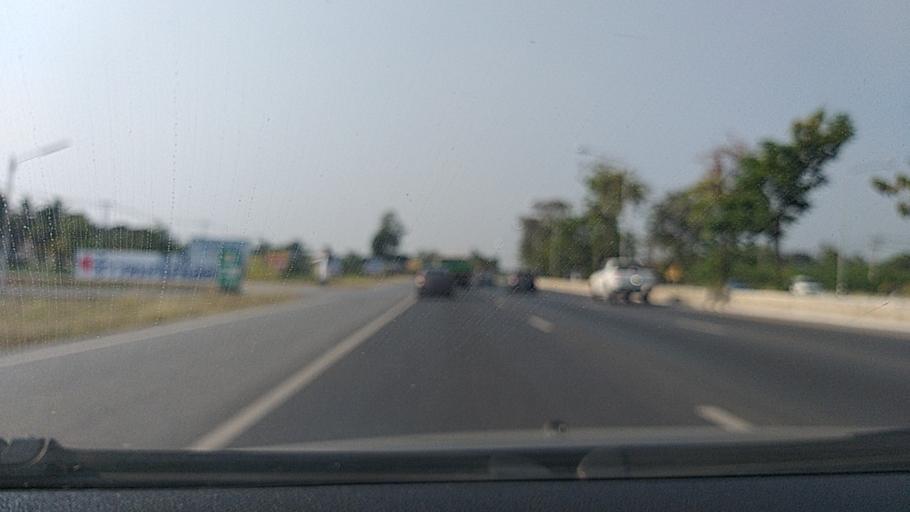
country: TH
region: Ang Thong
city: Chaiyo
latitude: 14.6817
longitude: 100.4661
